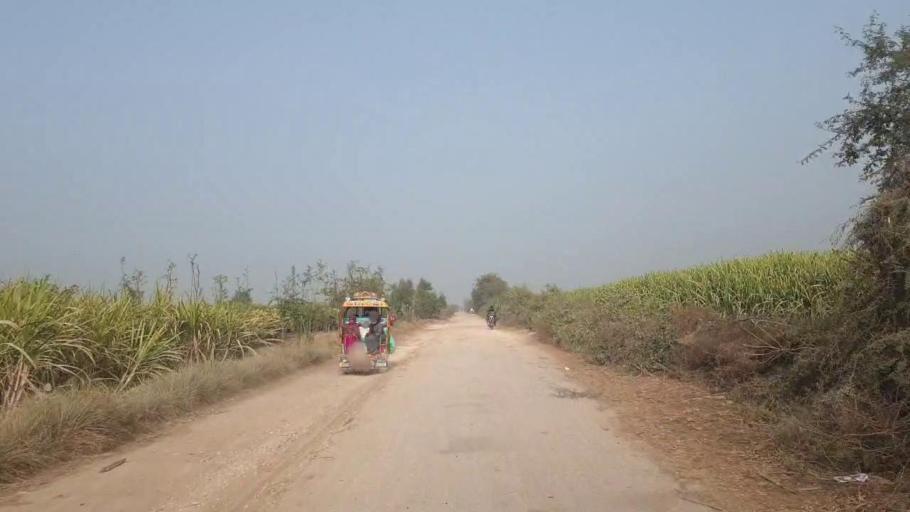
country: PK
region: Sindh
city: Shahdadpur
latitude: 25.8831
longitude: 68.5841
